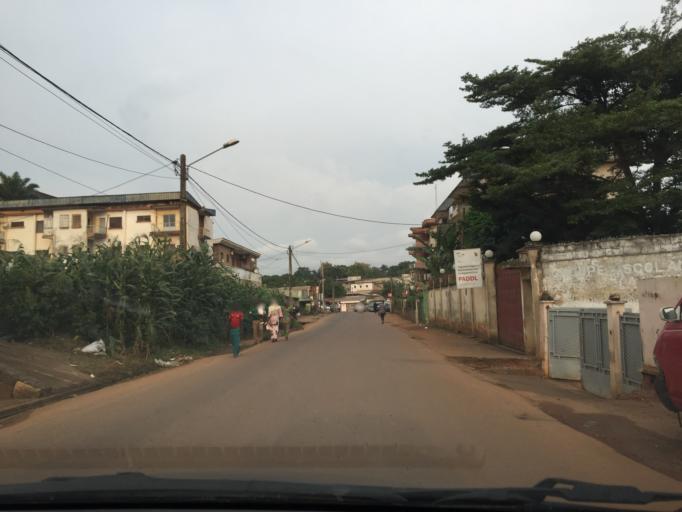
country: CM
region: Centre
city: Yaounde
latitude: 3.8852
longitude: 11.5164
